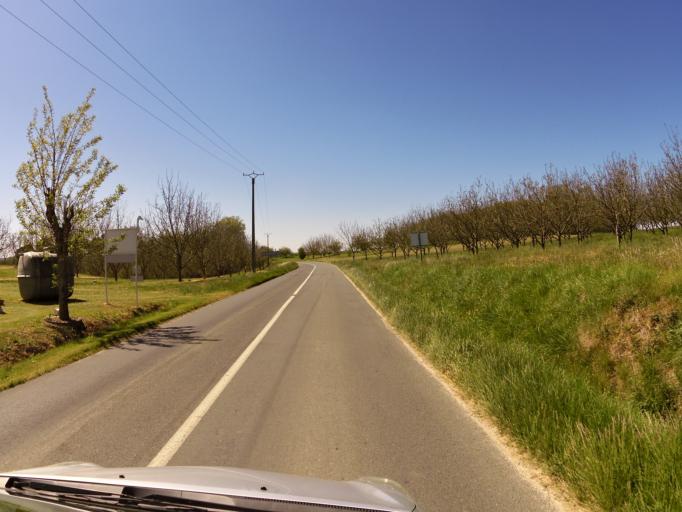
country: FR
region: Aquitaine
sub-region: Departement de la Dordogne
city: Eyvigues-et-Eybenes
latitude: 44.9735
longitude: 1.2919
